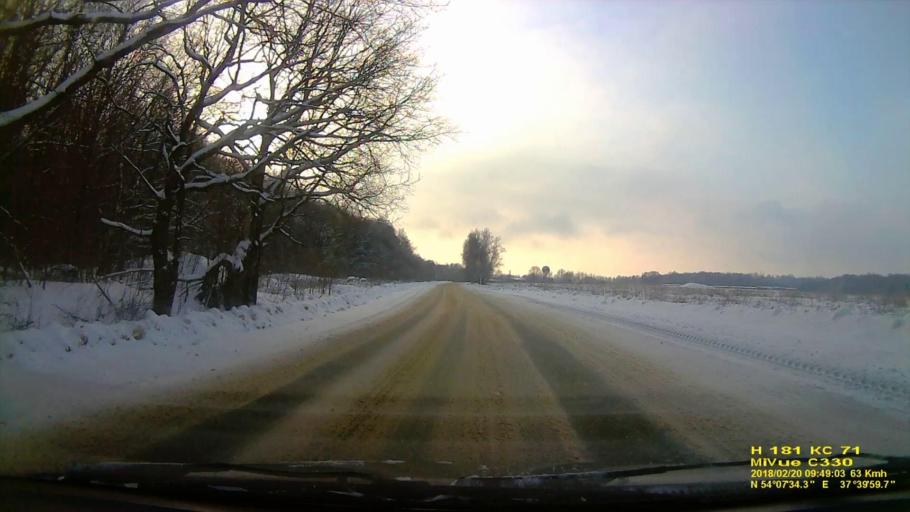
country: RU
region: Tula
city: Skuratovskiy
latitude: 54.1261
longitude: 37.6666
